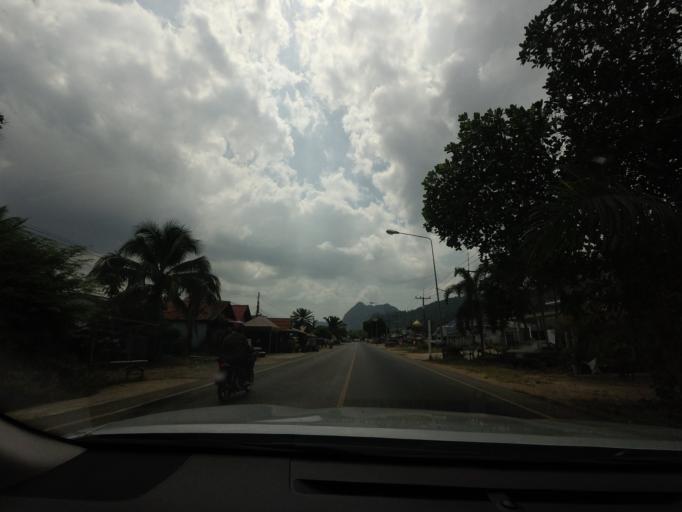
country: TH
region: Phangnga
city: Ban Ao Nang
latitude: 8.1092
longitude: 98.8028
